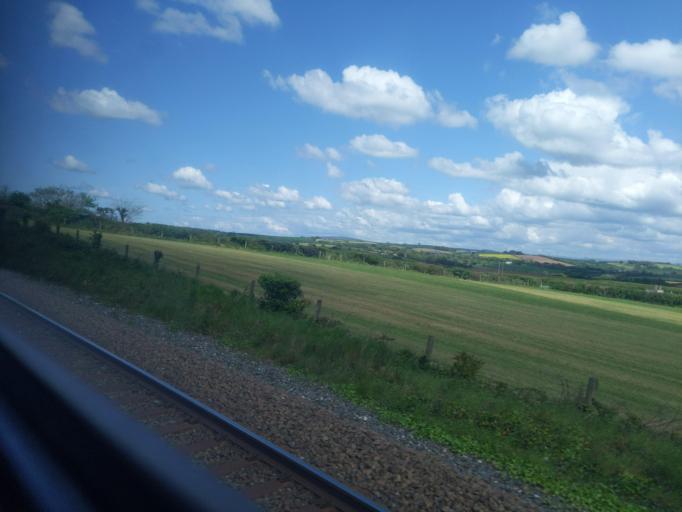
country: GB
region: England
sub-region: Cornwall
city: Pillaton
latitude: 50.4094
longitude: -4.3501
